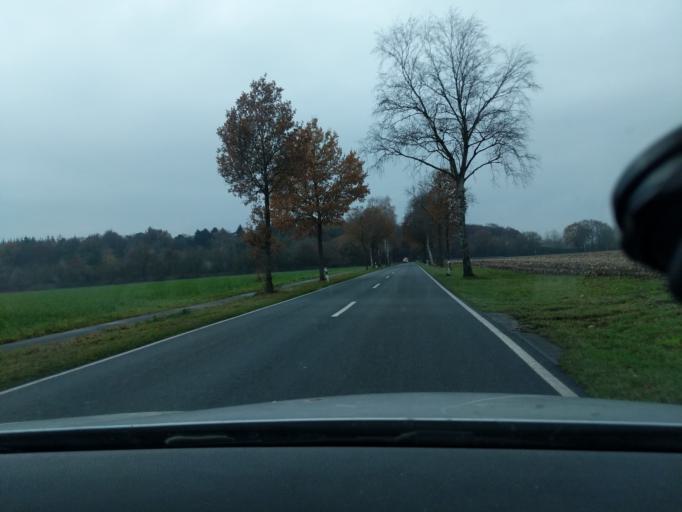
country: DE
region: Lower Saxony
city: Heeslingen
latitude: 53.3333
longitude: 9.3669
